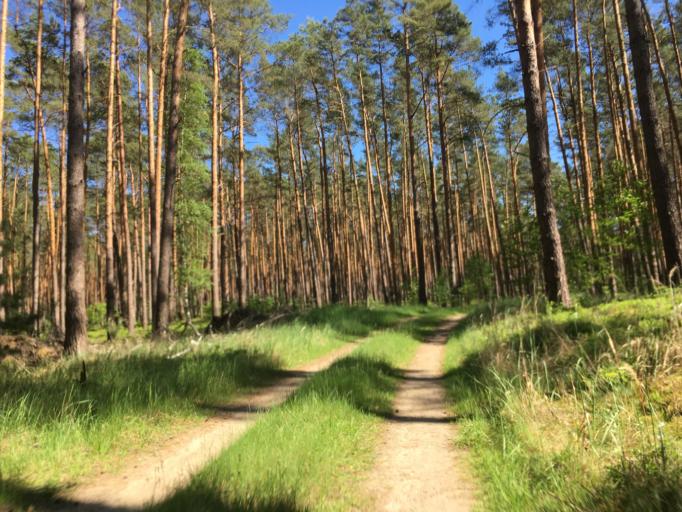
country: DE
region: Brandenburg
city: Joachimsthal
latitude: 52.9615
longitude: 13.6787
